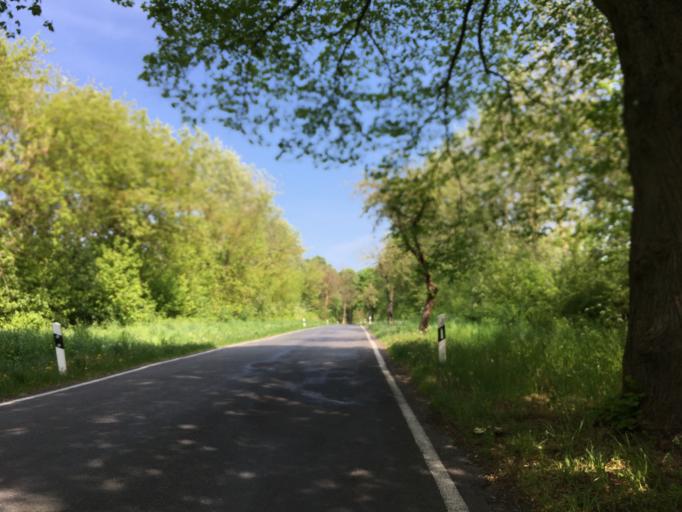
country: DE
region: Brandenburg
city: Werneuchen
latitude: 52.6641
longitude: 13.7317
